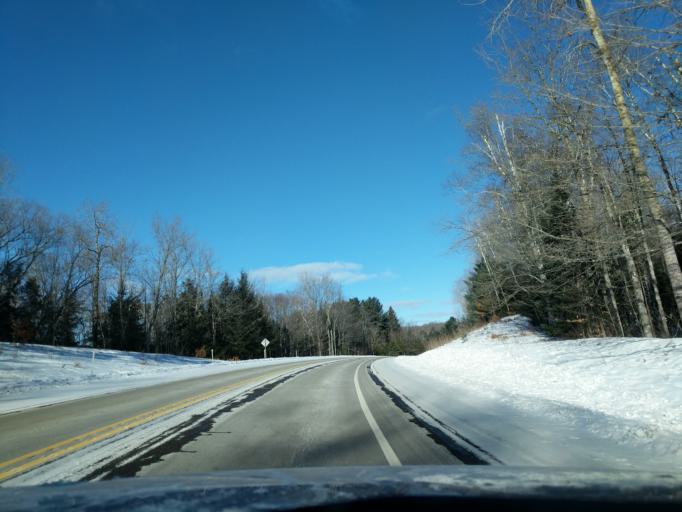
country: US
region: Wisconsin
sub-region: Menominee County
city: Keshena
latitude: 45.1212
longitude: -88.6638
